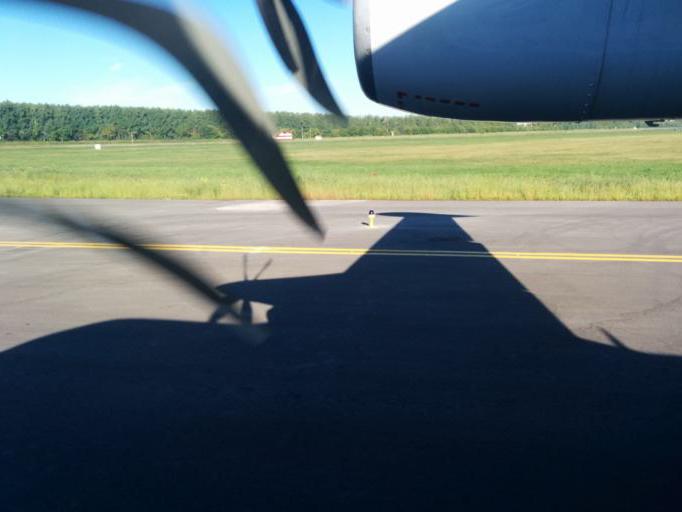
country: RU
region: Bashkortostan
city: Ufa
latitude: 54.5485
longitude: 55.8954
